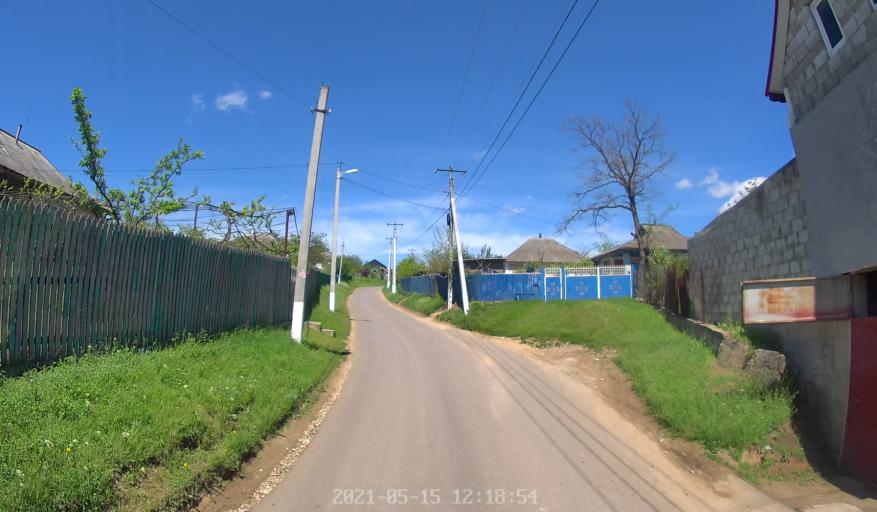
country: MD
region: Hincesti
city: Hincesti
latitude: 46.7992
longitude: 28.5415
